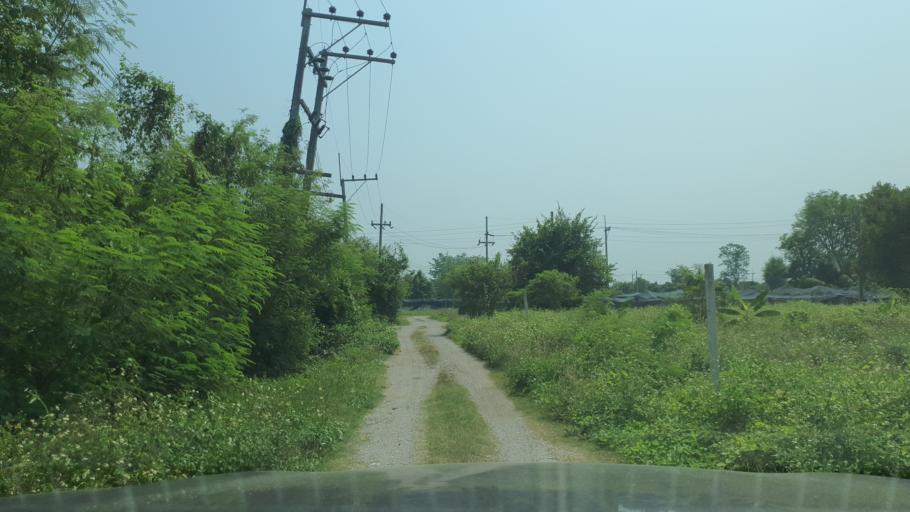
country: TH
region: Chiang Mai
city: Saraphi
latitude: 18.6707
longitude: 98.9926
